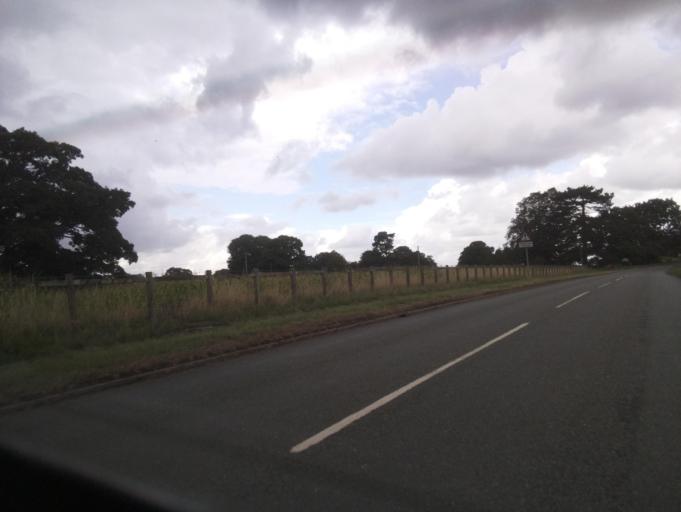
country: GB
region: England
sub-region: Staffordshire
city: Standon
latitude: 52.9135
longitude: -2.2243
